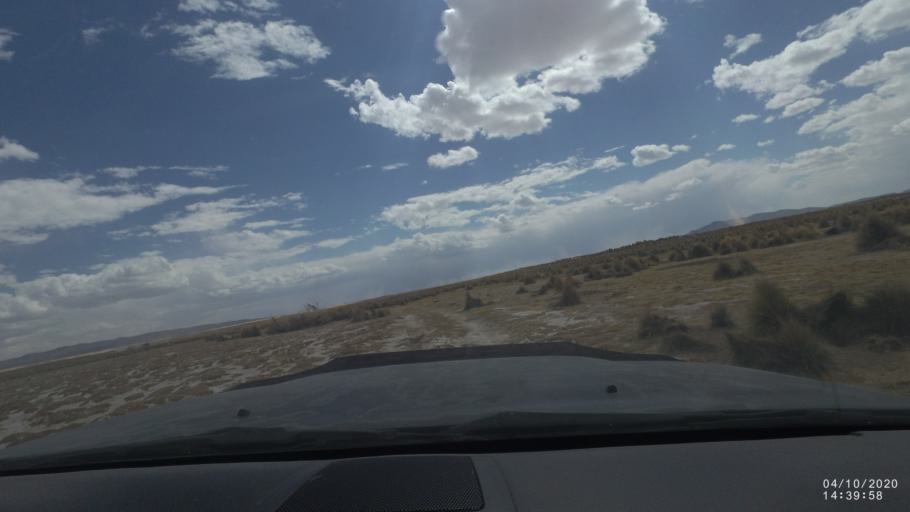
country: BO
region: Oruro
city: Poopo
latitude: -18.6782
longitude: -67.4890
